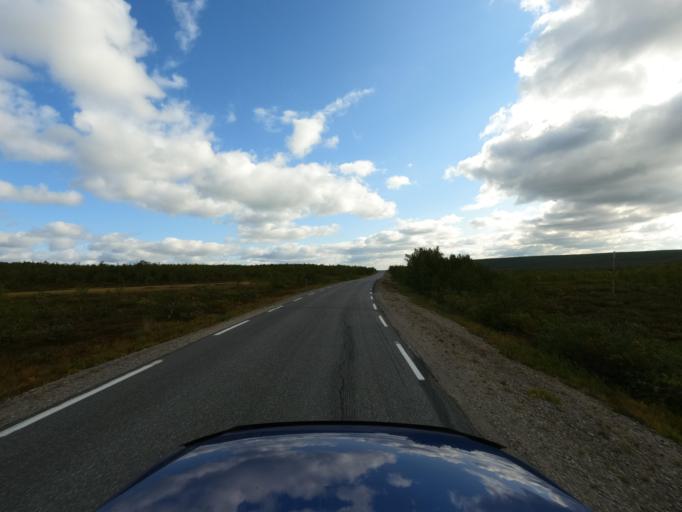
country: NO
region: Finnmark Fylke
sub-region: Porsanger
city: Lakselv
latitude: 69.3737
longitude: 24.3958
